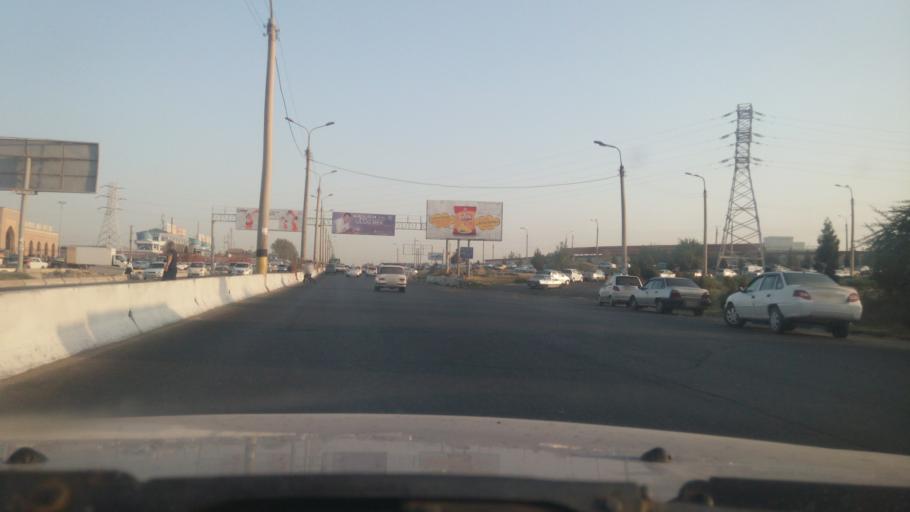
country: UZ
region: Toshkent Shahri
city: Tashkent
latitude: 41.2399
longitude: 69.1673
